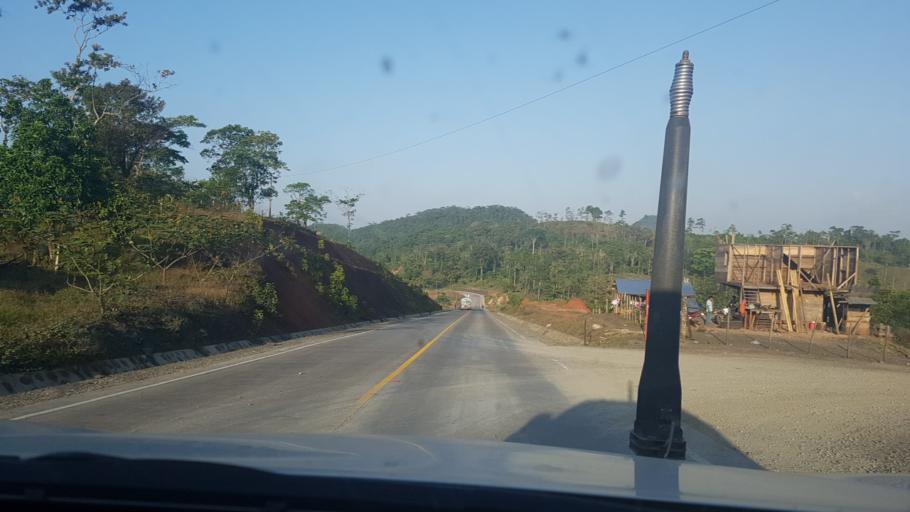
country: NI
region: Atlantico Sur
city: Rama
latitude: 11.8200
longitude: -84.0919
